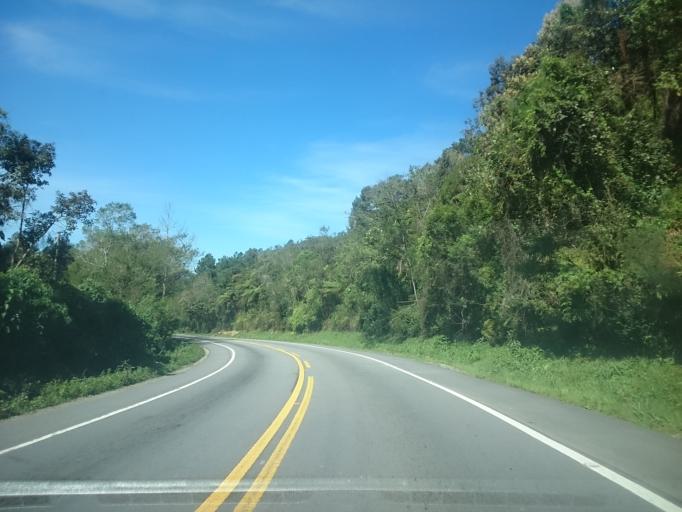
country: BR
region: Santa Catarina
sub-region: Santo Amaro Da Imperatriz
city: Santo Amaro da Imperatriz
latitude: -27.6942
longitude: -48.9701
